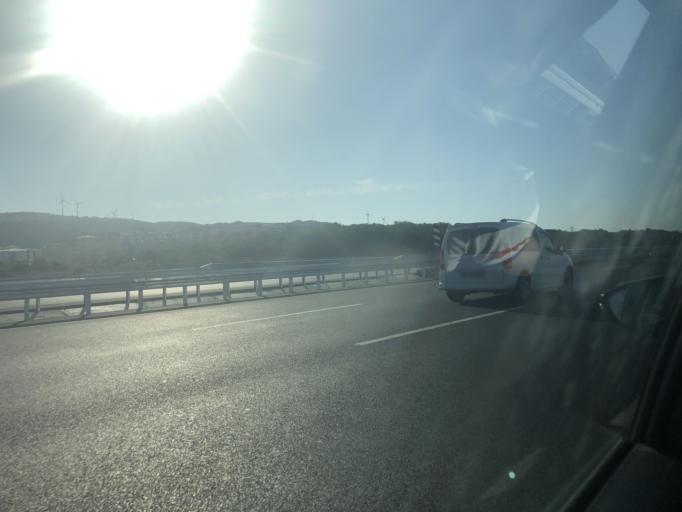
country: TR
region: Istanbul
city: Catalca
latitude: 41.1421
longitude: 28.4781
